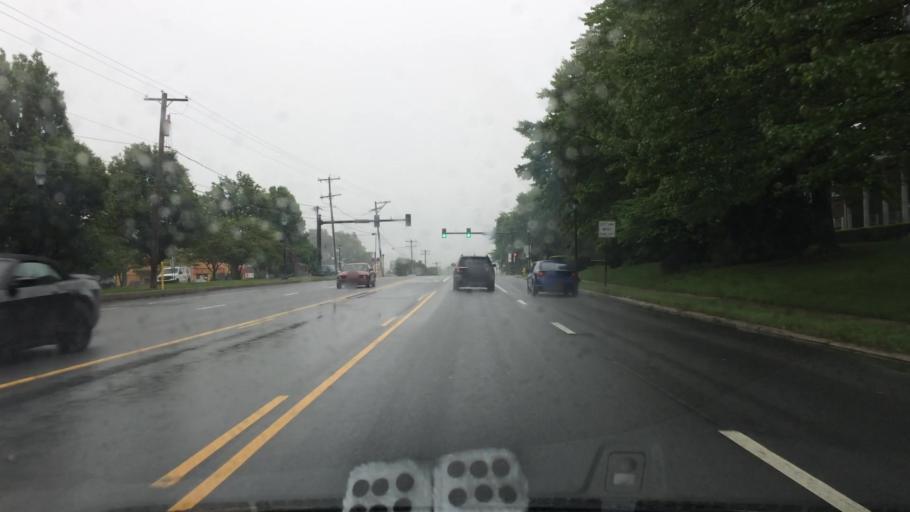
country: US
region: Pennsylvania
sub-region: Delaware County
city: Village Green-Green Ridge
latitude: 39.8614
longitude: -75.4275
